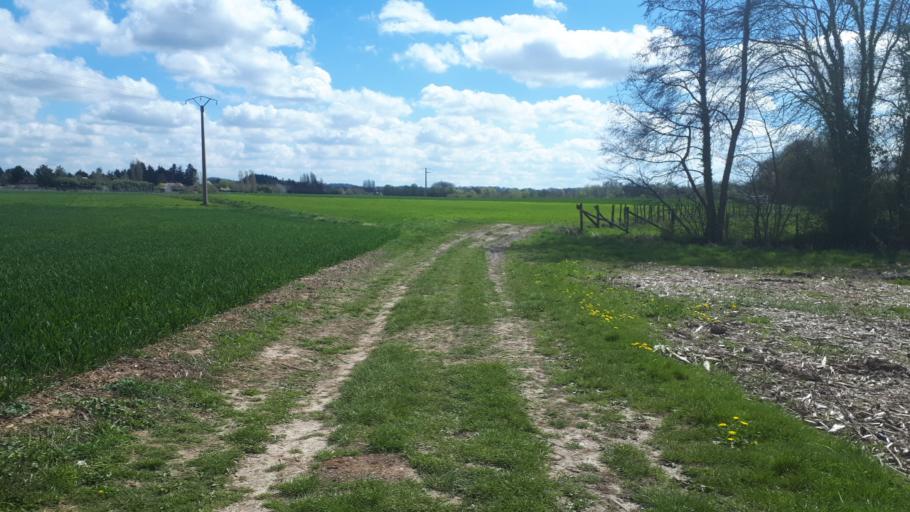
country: FR
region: Centre
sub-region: Departement du Loir-et-Cher
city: Villiers-sur-Loir
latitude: 47.7935
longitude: 0.9898
